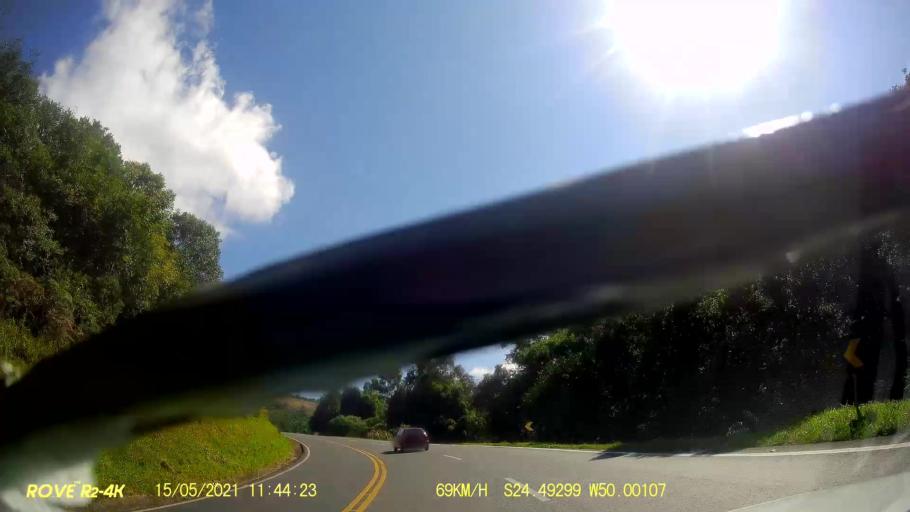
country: BR
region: Parana
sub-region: Pirai Do Sul
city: Pirai do Sul
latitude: -24.4930
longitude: -50.0011
